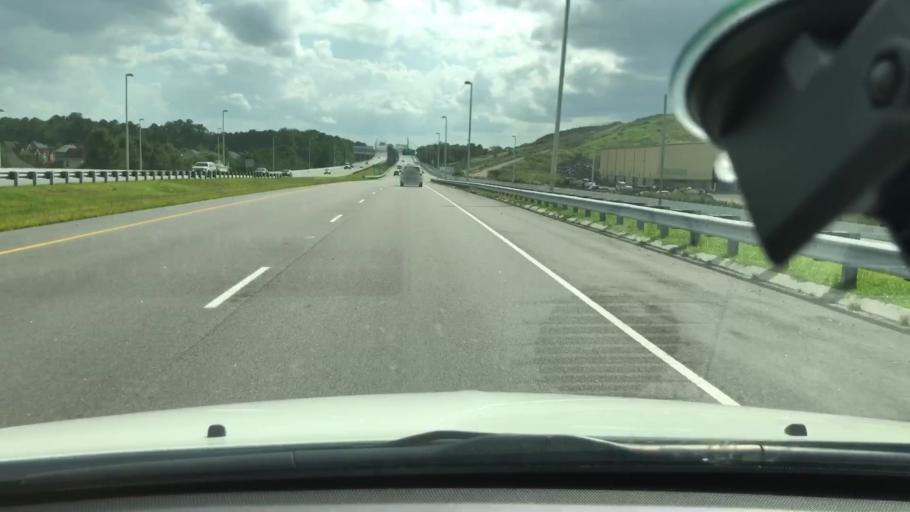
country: US
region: Virginia
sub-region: City of Chesapeake
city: Chesapeake
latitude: 36.7473
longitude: -76.2848
